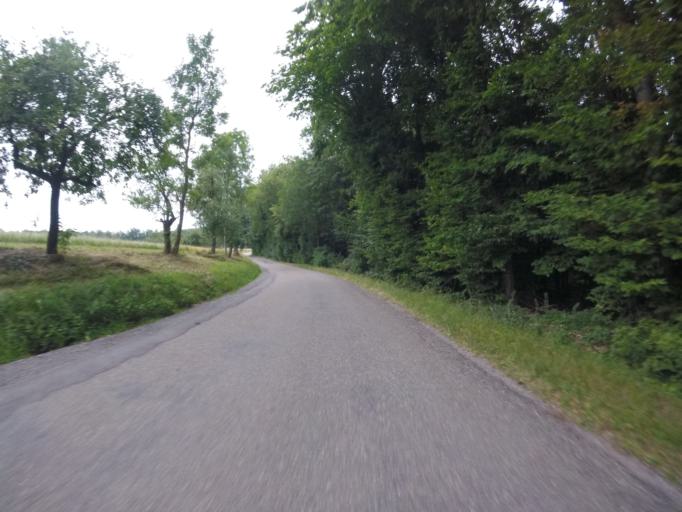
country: DE
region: Baden-Wuerttemberg
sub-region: Regierungsbezirk Stuttgart
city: Oberstenfeld
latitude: 49.0122
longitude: 9.3647
